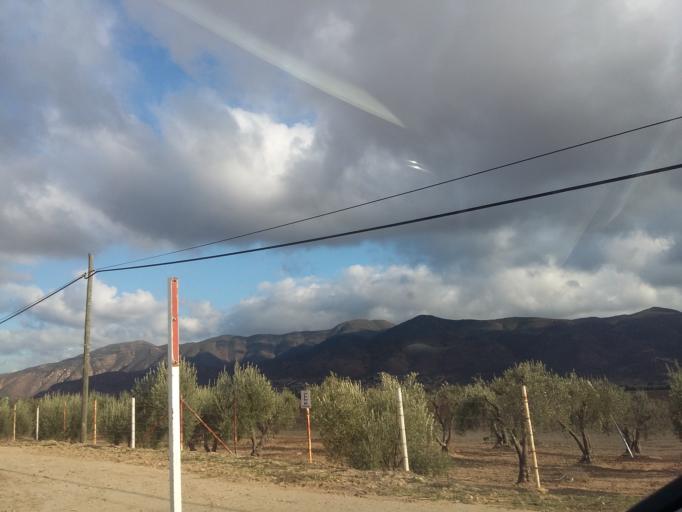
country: MX
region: Baja California
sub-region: Ensenada
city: Rancho Verde
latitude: 32.0859
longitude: -116.5975
